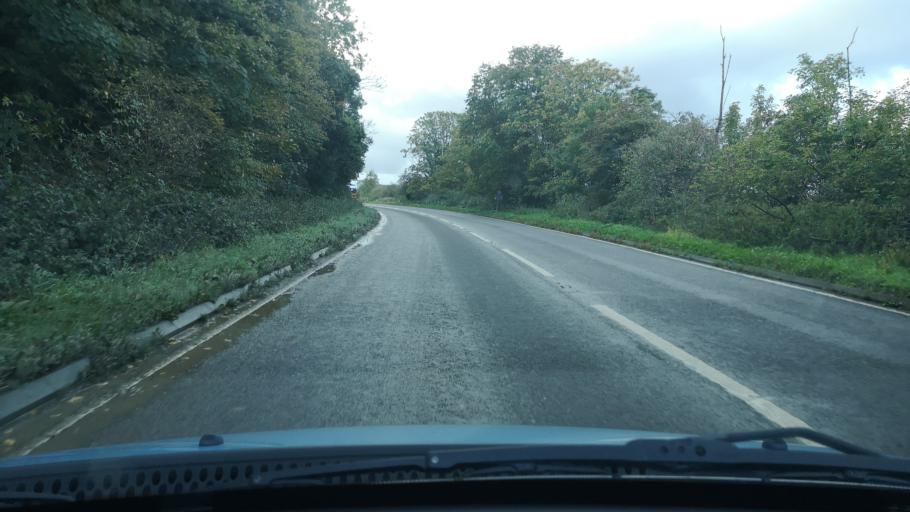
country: GB
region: England
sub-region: North Lincolnshire
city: Crowle
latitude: 53.5873
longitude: -0.8248
